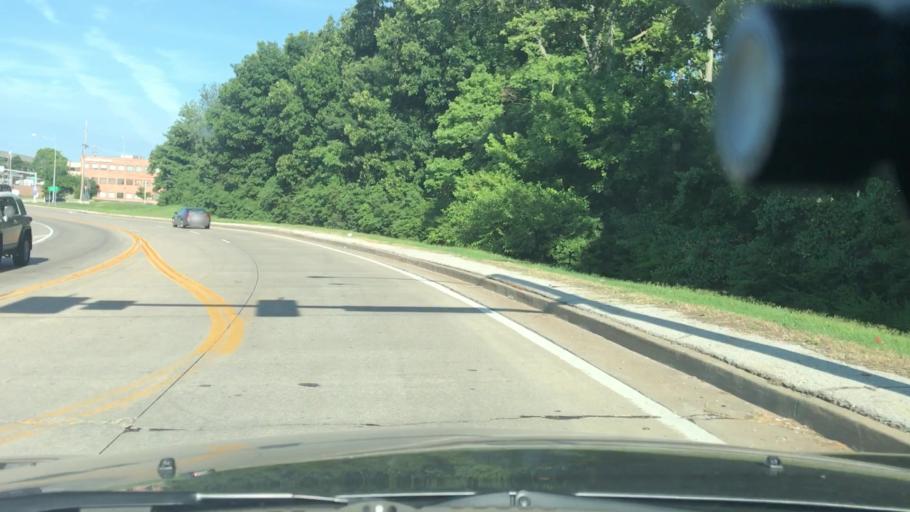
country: US
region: Missouri
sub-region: Saint Louis County
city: Frontenac
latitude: 38.6405
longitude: -90.4411
